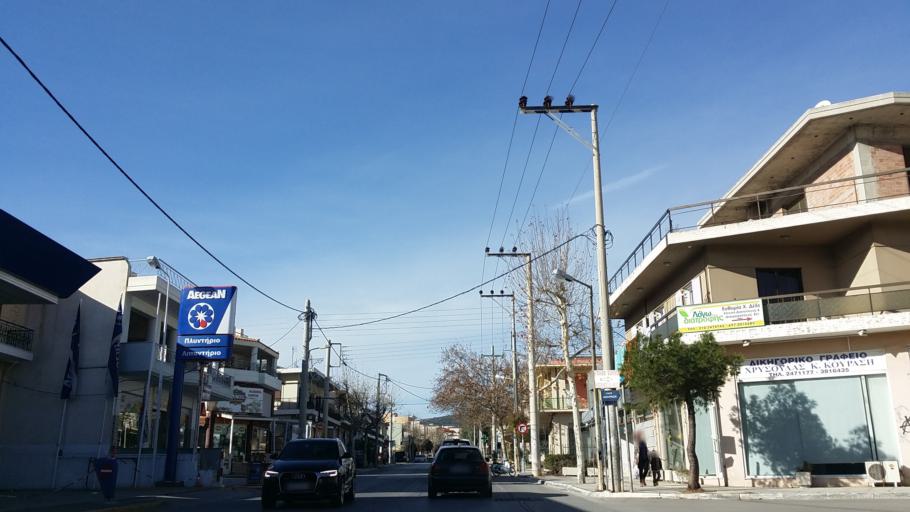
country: GR
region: Attica
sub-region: Nomarchia Dytikis Attikis
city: Ano Liosia
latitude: 38.0789
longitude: 23.7001
